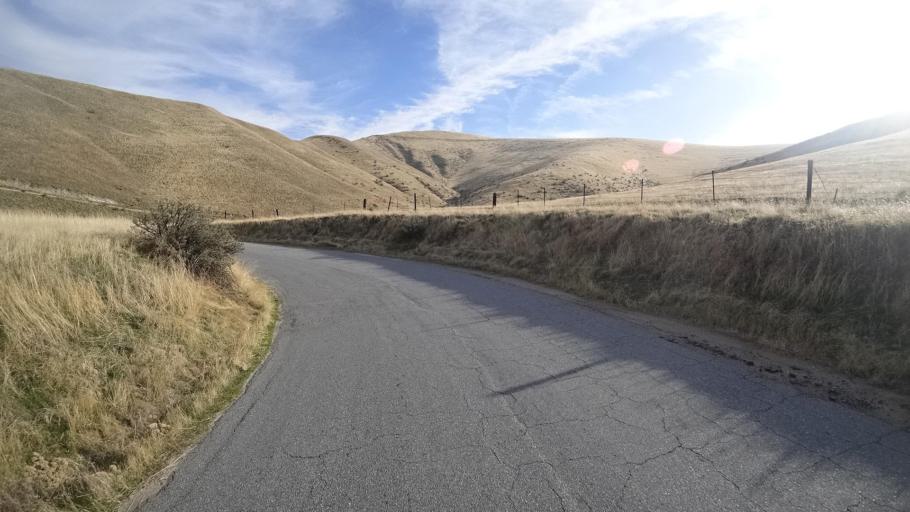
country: US
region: California
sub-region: Kern County
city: Bear Valley Springs
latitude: 35.2804
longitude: -118.6743
